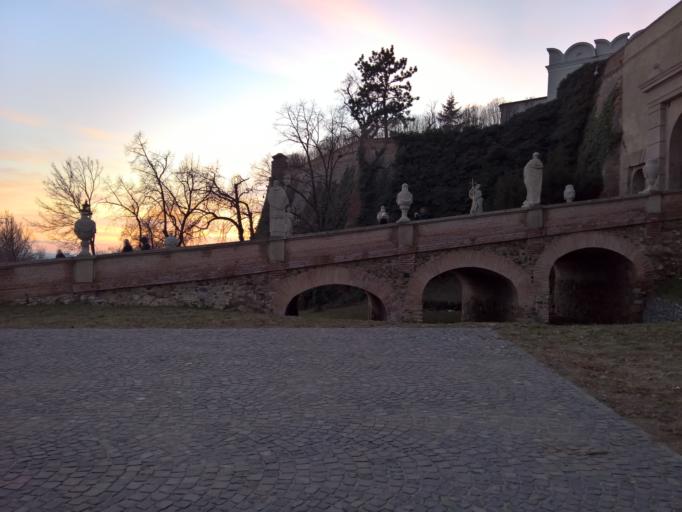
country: SK
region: Nitriansky
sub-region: Okres Nitra
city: Nitra
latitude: 48.3181
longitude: 18.0878
